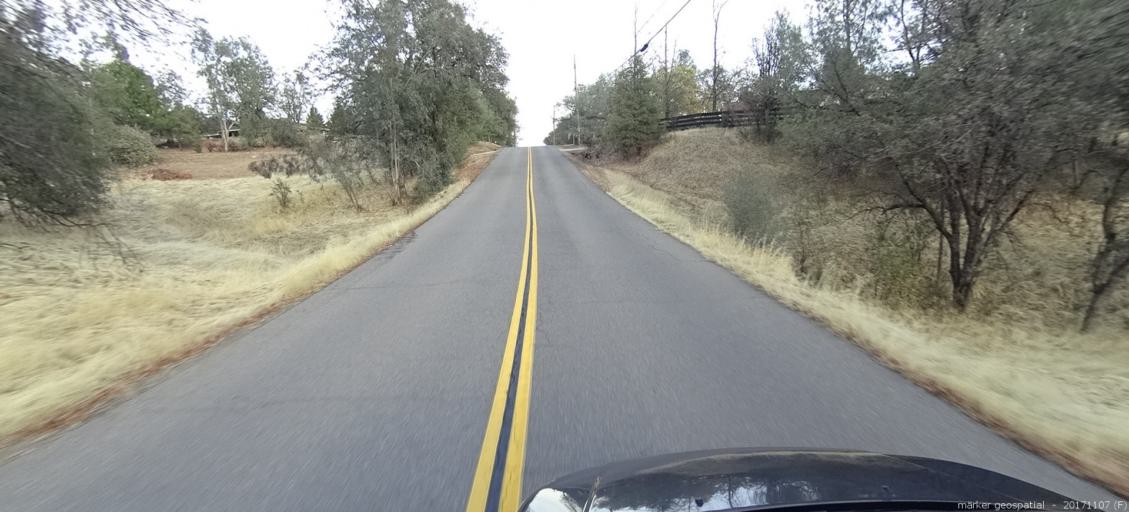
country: US
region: California
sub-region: Shasta County
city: Shasta
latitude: 40.5415
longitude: -122.4815
